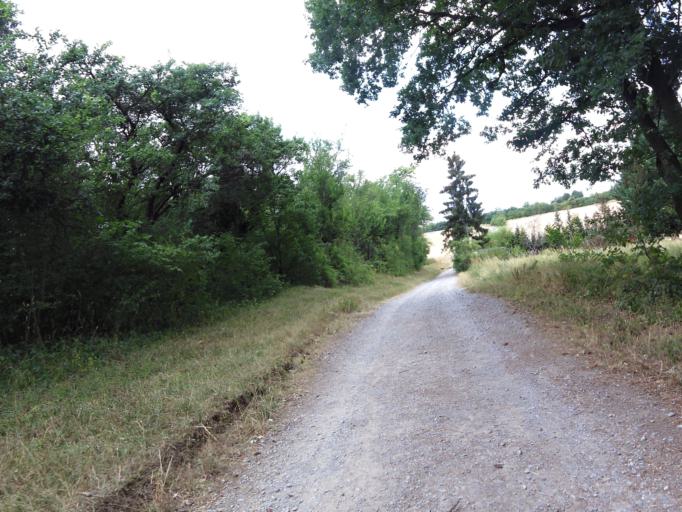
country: DE
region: Bavaria
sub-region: Regierungsbezirk Unterfranken
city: Gerbrunn
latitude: 49.7731
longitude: 9.9900
